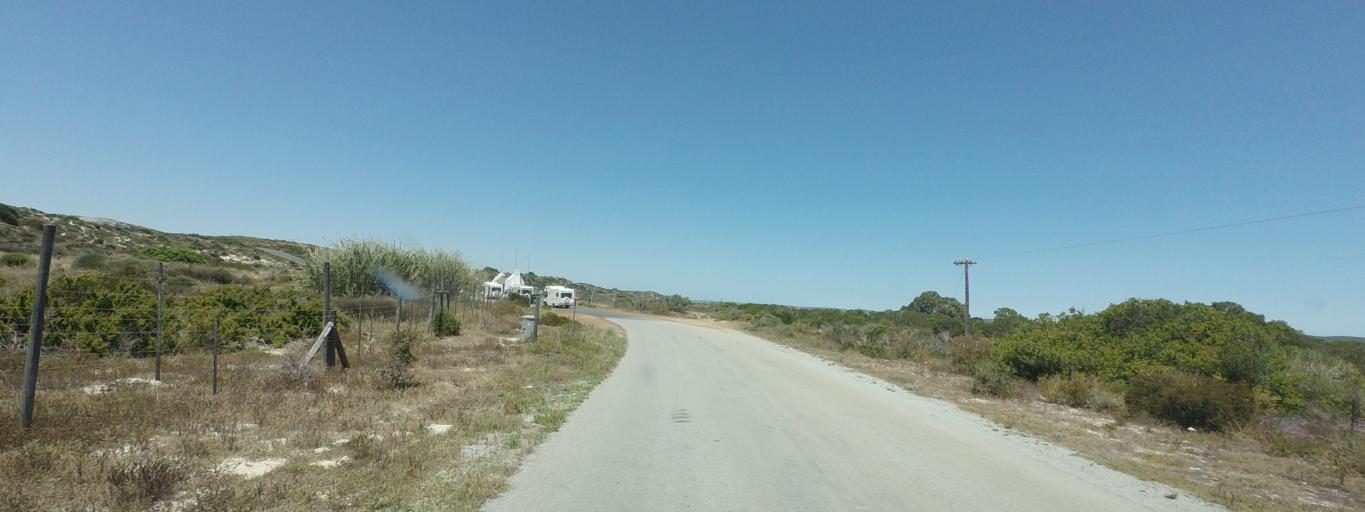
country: ZA
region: Western Cape
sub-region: West Coast District Municipality
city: Saldanha
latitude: -33.1170
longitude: 18.0543
